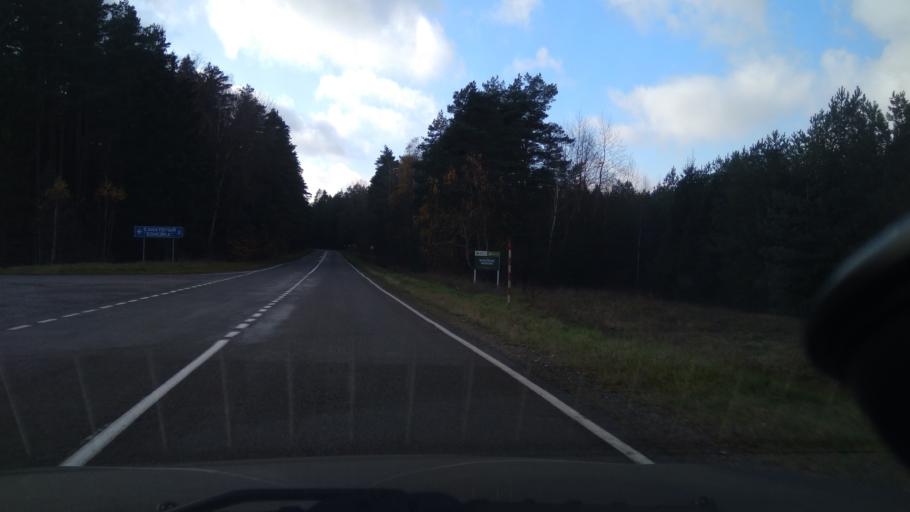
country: BY
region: Minsk
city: Slutsk
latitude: 53.2298
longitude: 27.6249
